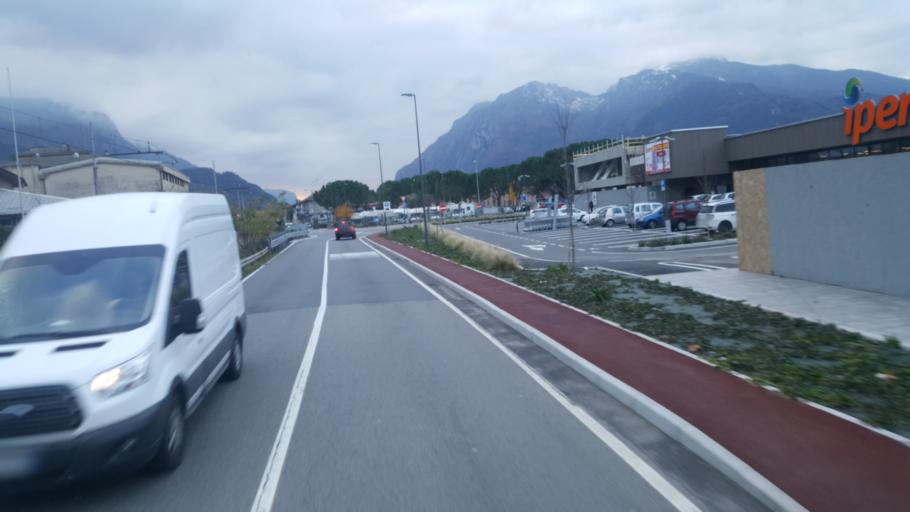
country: IT
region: Lombardy
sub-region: Provincia di Lecco
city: Mandello del Lario
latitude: 45.9198
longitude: 9.3145
